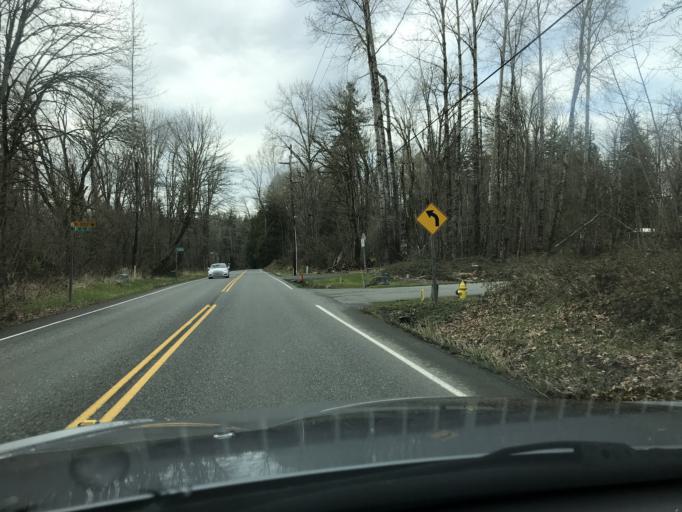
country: US
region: Washington
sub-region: King County
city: Union Hill-Novelty Hill
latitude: 47.6598
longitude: -122.0040
